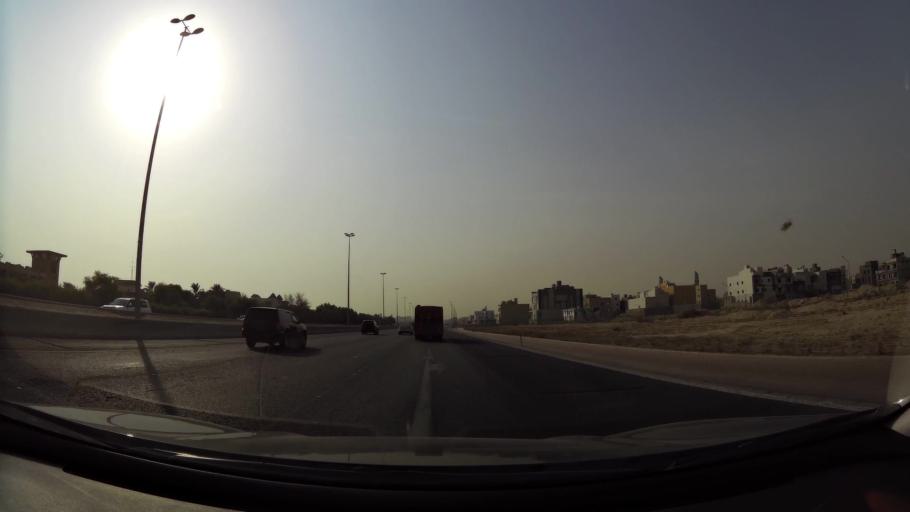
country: KW
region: Mubarak al Kabir
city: Mubarak al Kabir
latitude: 29.2025
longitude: 48.1062
